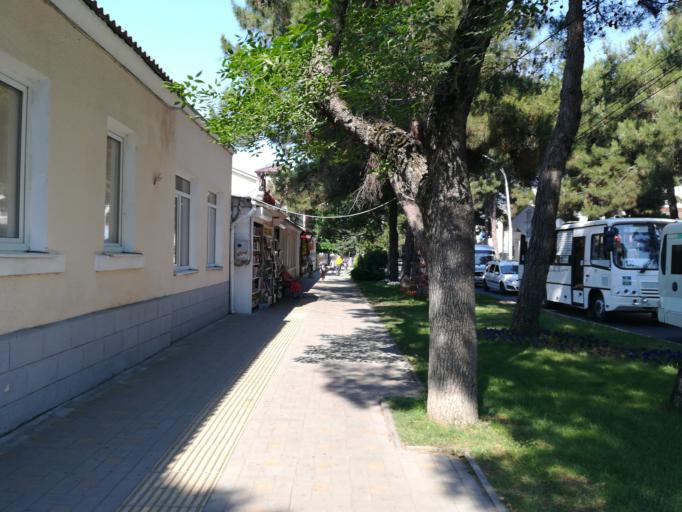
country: RU
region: Krasnodarskiy
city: Anapa
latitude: 44.8948
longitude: 37.3182
